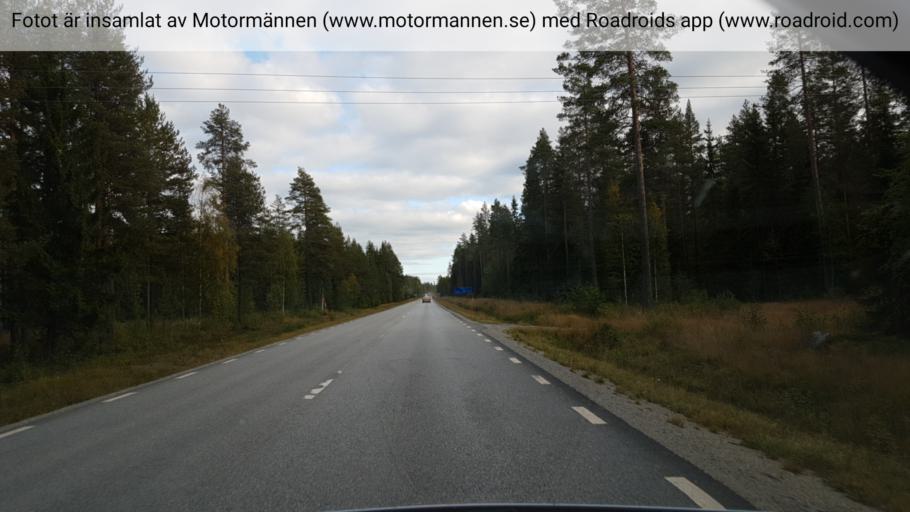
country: SE
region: Vaesterbotten
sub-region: Vindelns Kommun
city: Vindeln
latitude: 64.0874
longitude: 19.6212
